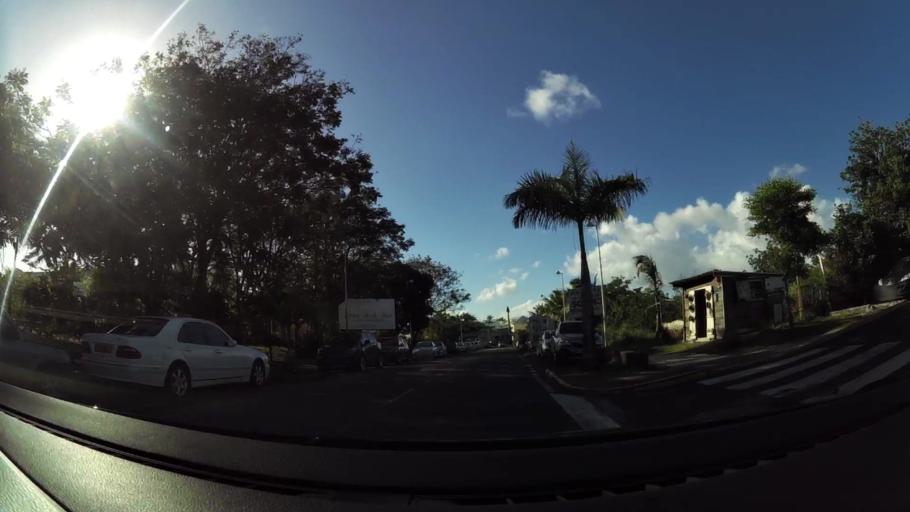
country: GP
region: Guadeloupe
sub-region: Guadeloupe
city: Le Gosier
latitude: 16.2080
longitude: -61.5045
